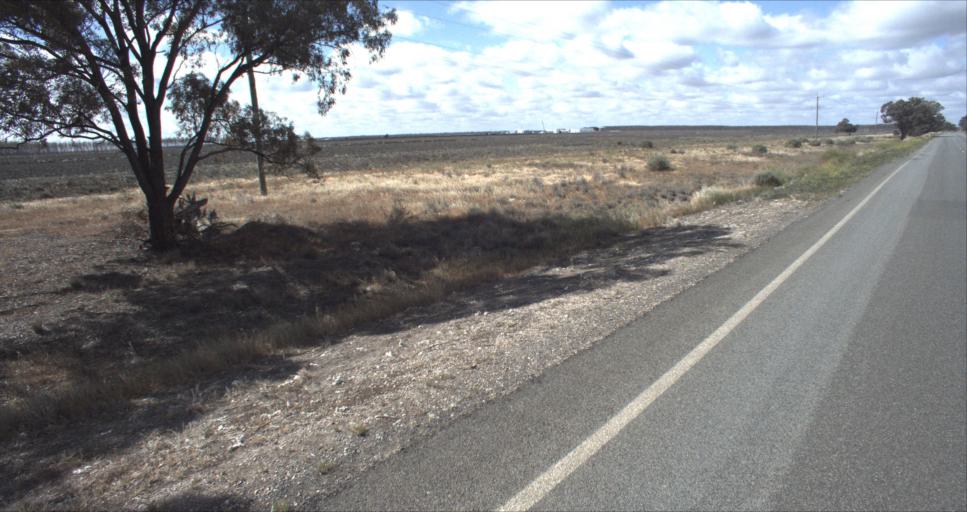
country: AU
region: New South Wales
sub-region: Murrumbidgee Shire
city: Darlington Point
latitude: -34.5599
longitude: 146.1692
